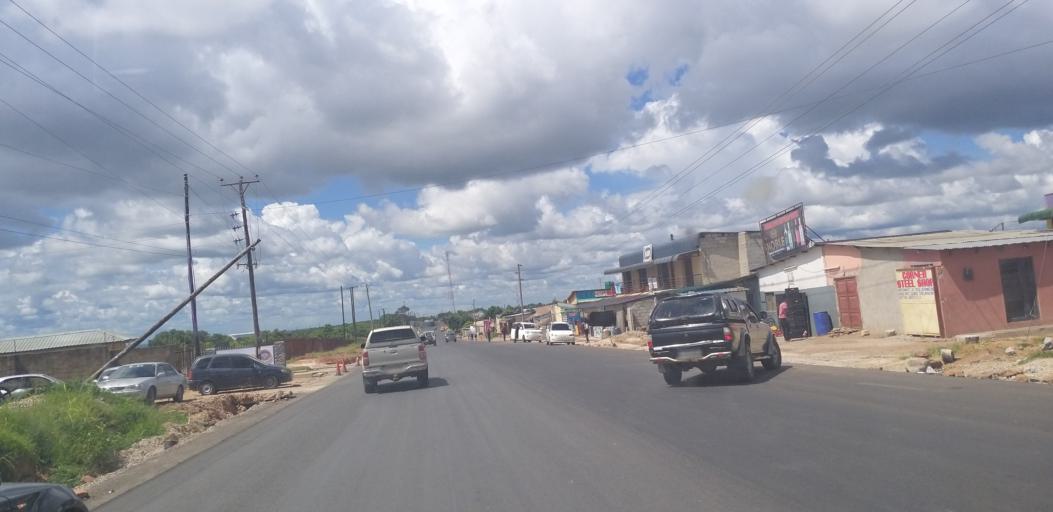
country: ZM
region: Lusaka
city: Lusaka
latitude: -15.3649
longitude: 28.3207
